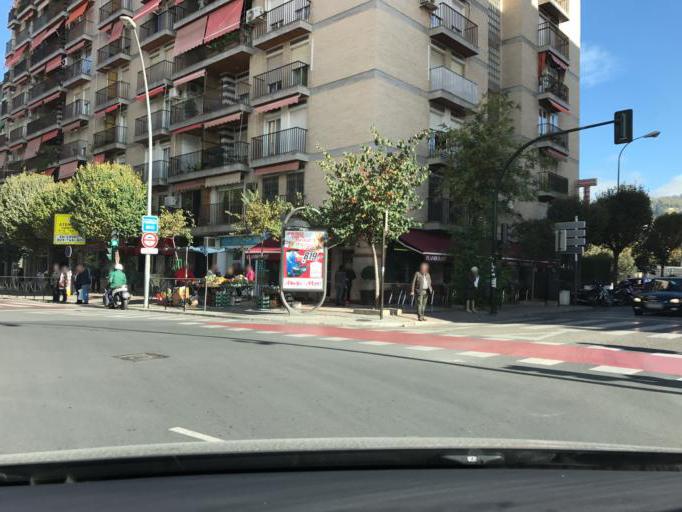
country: ES
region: Andalusia
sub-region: Provincia de Granada
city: Granada
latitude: 37.1651
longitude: -3.5941
